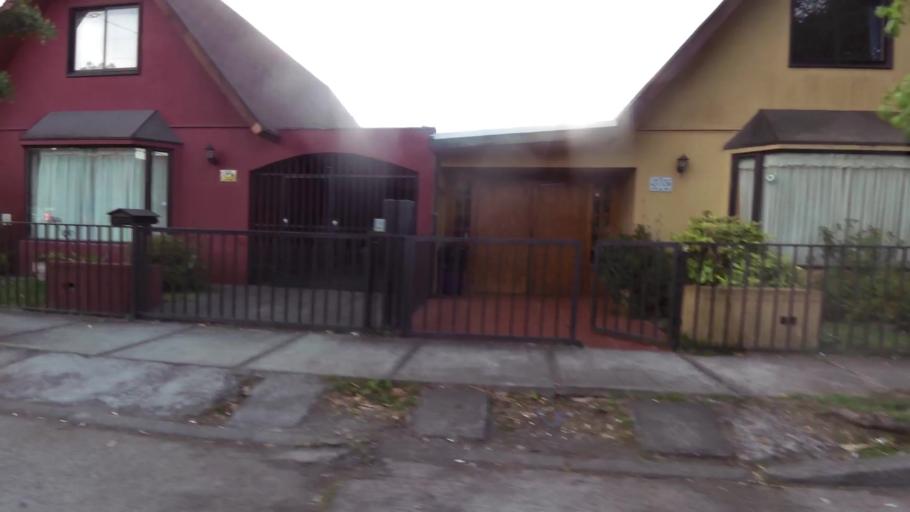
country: CL
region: Biobio
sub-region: Provincia de Concepcion
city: Concepcion
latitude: -36.8422
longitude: -73.0941
